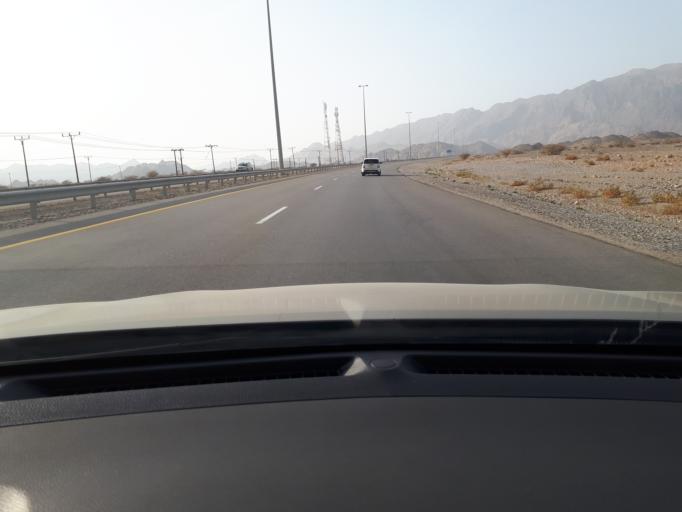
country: OM
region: Muhafazat Masqat
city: Muscat
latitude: 23.2906
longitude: 58.7424
